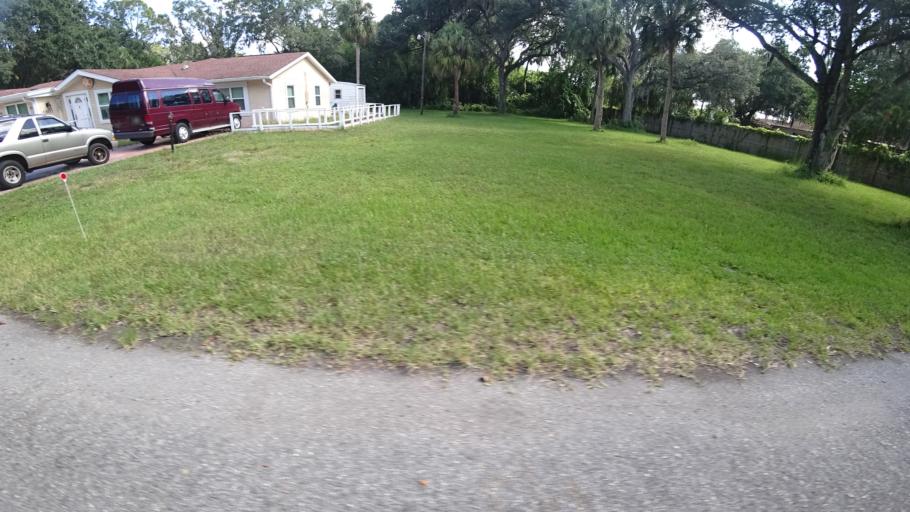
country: US
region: Florida
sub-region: Manatee County
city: Ellenton
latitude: 27.4900
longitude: -82.4764
